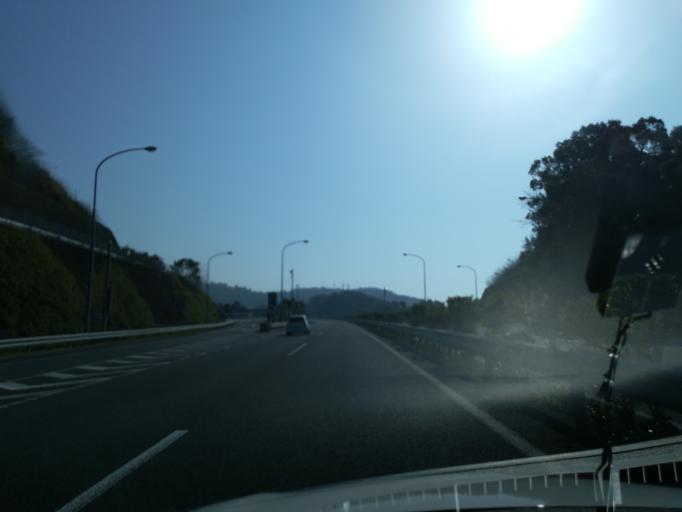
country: JP
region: Kochi
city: Kochi-shi
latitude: 33.6015
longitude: 133.6128
